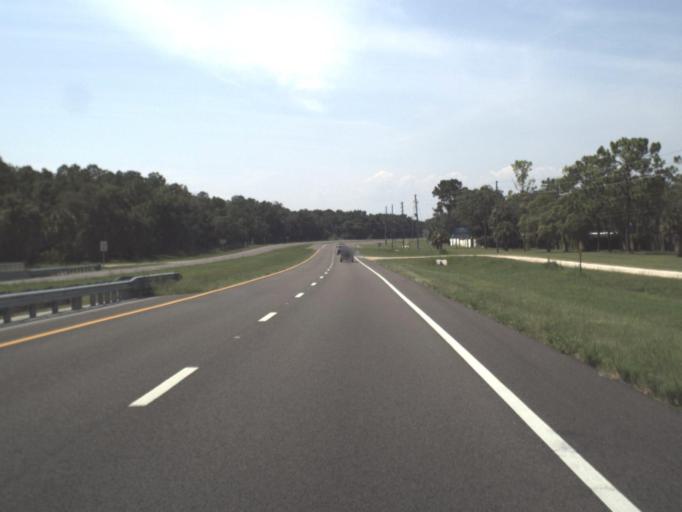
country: US
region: Florida
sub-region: Levy County
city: Inglis
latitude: 29.0165
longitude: -82.6659
